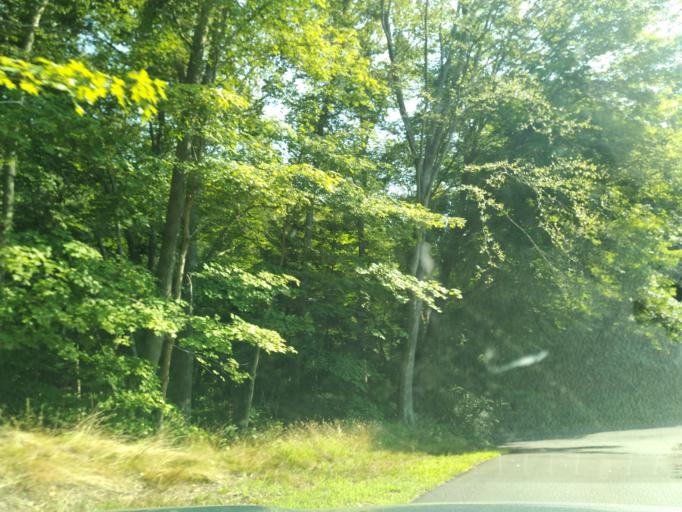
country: US
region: Connecticut
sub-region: New Haven County
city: Southbury
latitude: 41.4207
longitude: -73.2047
